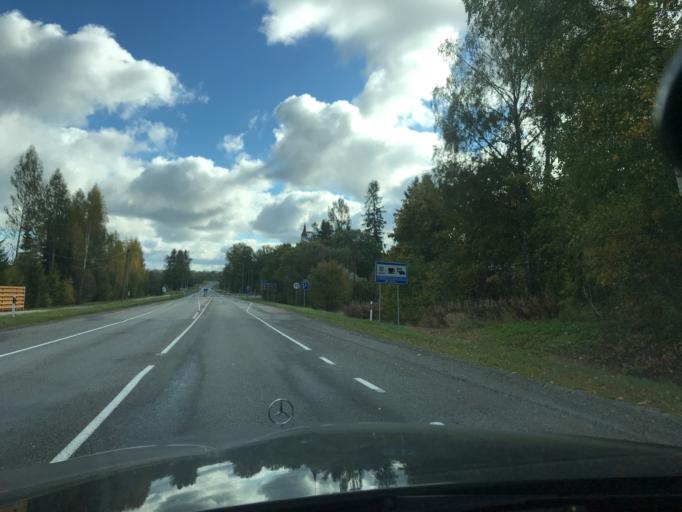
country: EE
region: Vorumaa
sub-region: Antsla vald
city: Vana-Antsla
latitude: 57.9273
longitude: 26.3288
